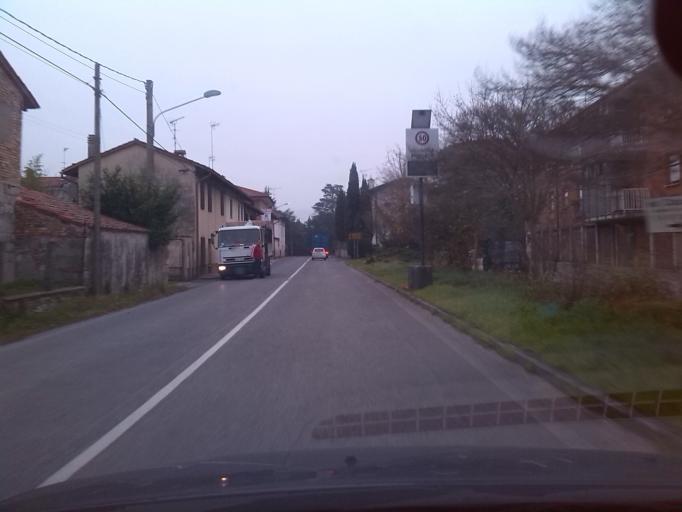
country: IT
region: Friuli Venezia Giulia
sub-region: Provincia di Gorizia
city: Gradisca d'Isonzo
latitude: 45.8978
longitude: 13.4992
